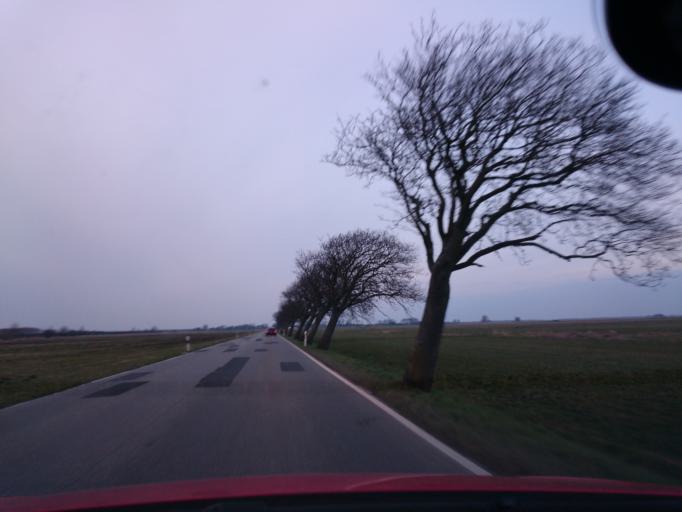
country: DE
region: Mecklenburg-Vorpommern
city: Zingst
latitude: 54.3855
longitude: 12.6776
